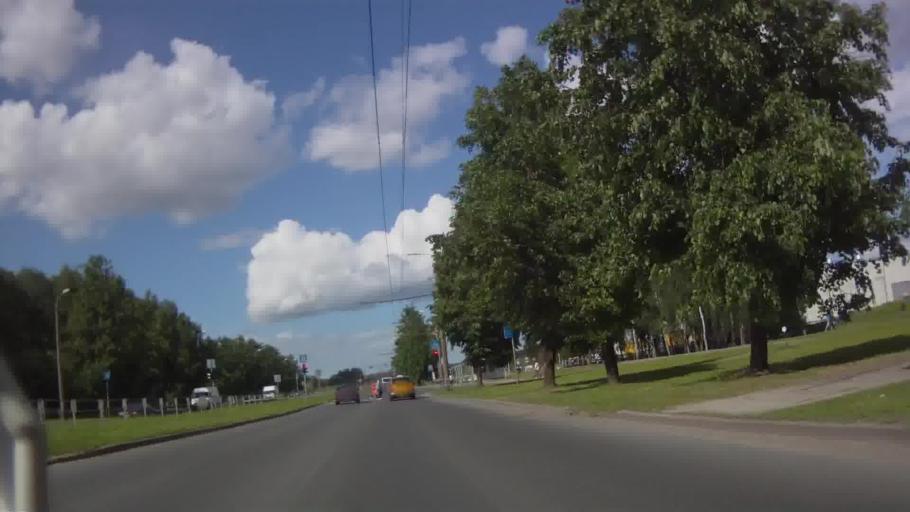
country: LV
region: Stopini
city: Ulbroka
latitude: 56.9438
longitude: 24.2061
